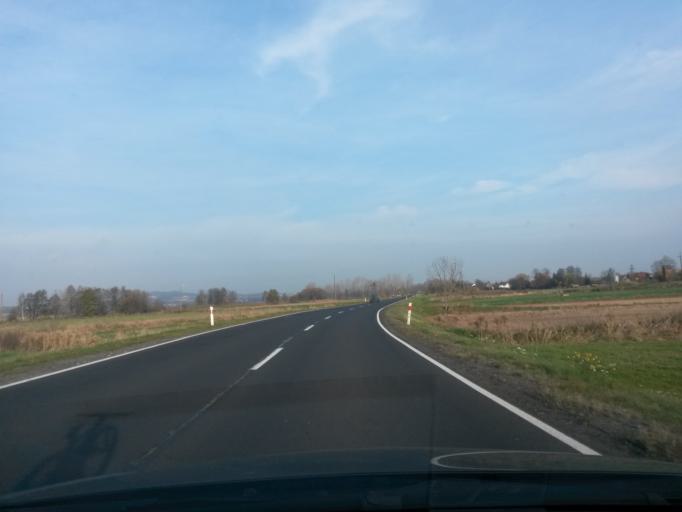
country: PL
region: Lower Silesian Voivodeship
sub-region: Powiat swidnicki
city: Strzegom
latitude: 50.9302
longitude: 16.3036
